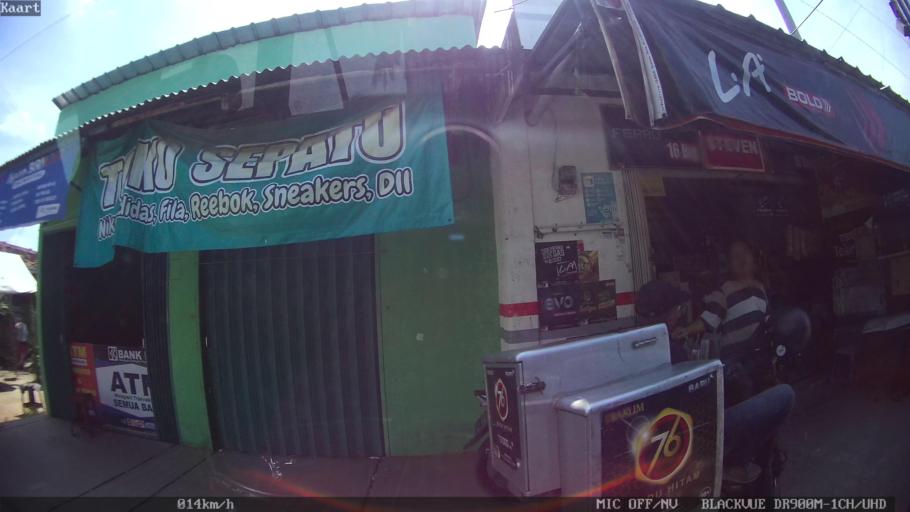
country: ID
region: Lampung
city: Kedaton
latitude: -5.3740
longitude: 105.2598
